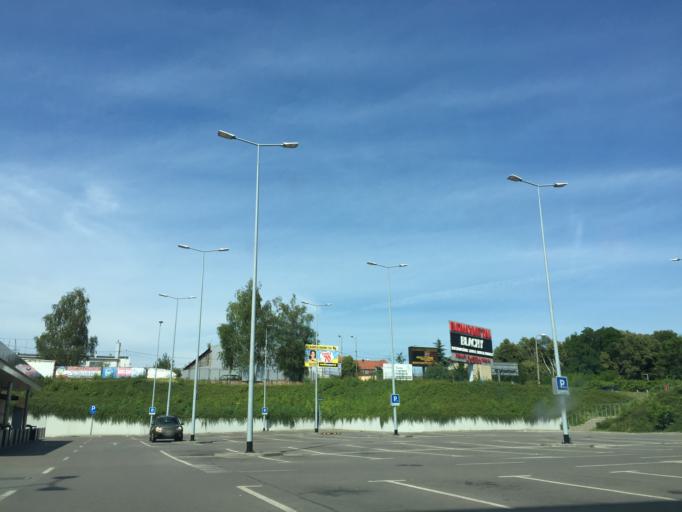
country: PL
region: Silesian Voivodeship
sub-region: Piekary Slaskie
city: Piekary Slaskie
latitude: 50.3694
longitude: 18.9435
